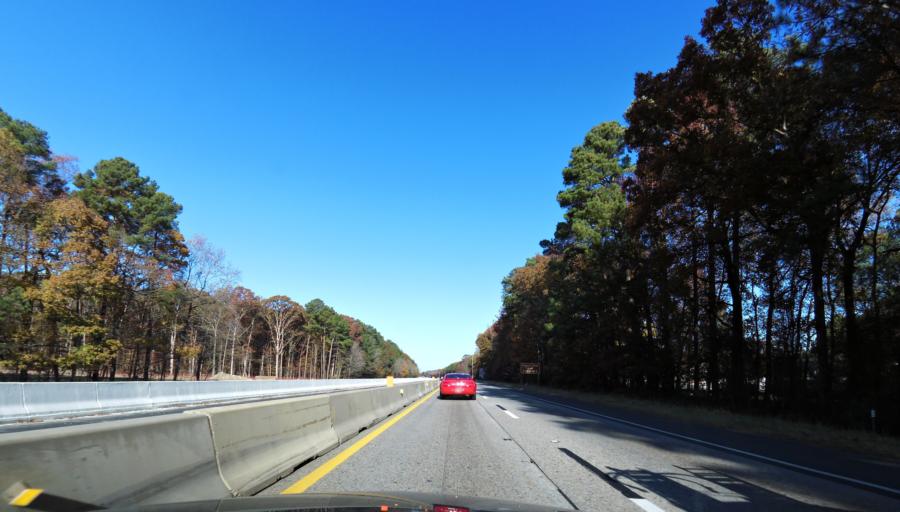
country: US
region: Virginia
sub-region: York County
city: Yorktown
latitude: 37.1501
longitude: -76.5350
